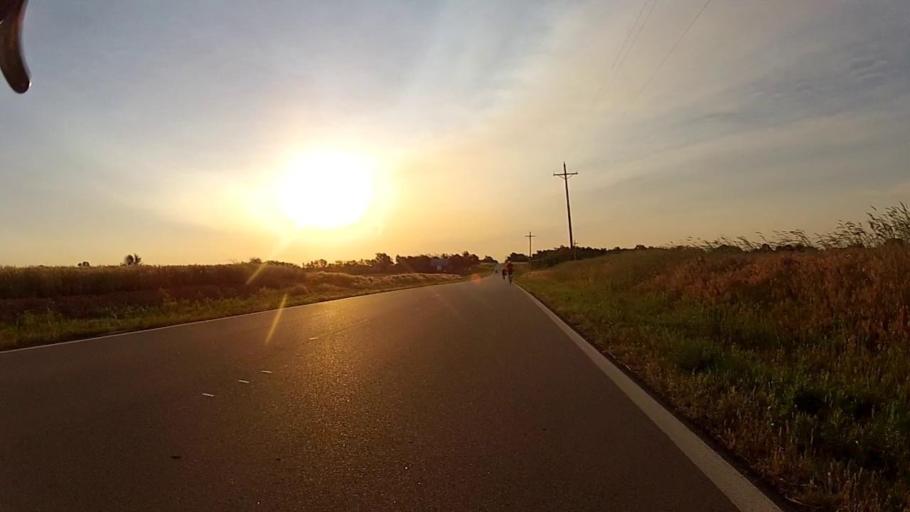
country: US
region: Kansas
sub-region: Harper County
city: Anthony
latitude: 37.1526
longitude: -97.9616
